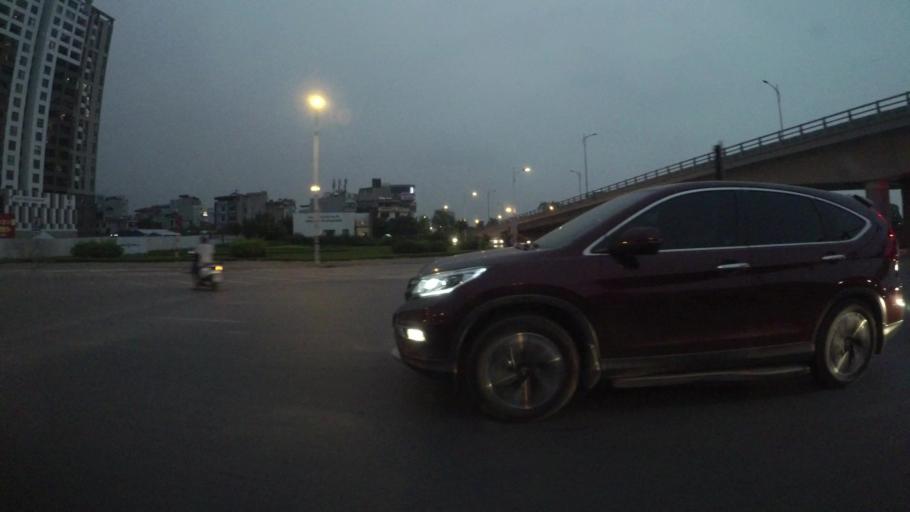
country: VN
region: Ha Noi
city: Trau Quy
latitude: 21.0268
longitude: 105.8962
